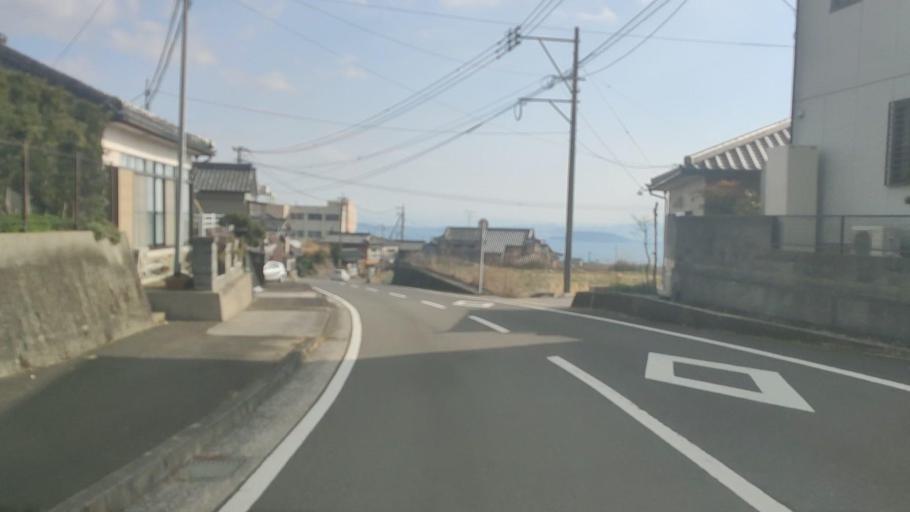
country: JP
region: Nagasaki
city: Shimabara
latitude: 32.6780
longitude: 130.2793
